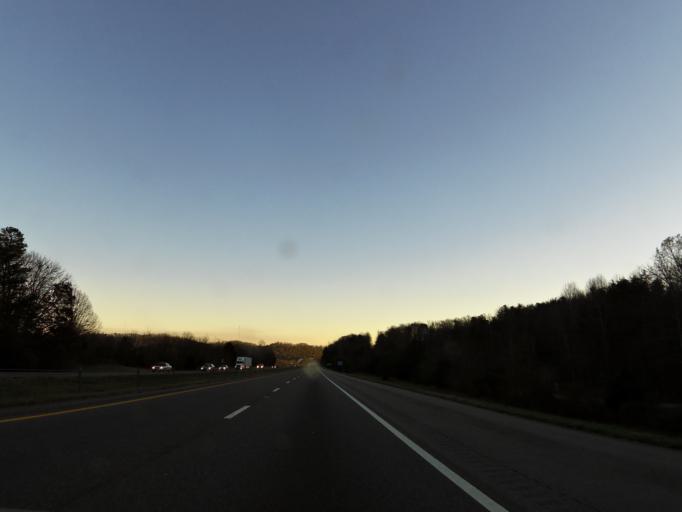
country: US
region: Tennessee
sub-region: Anderson County
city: Clinton
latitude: 36.0603
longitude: -84.0073
